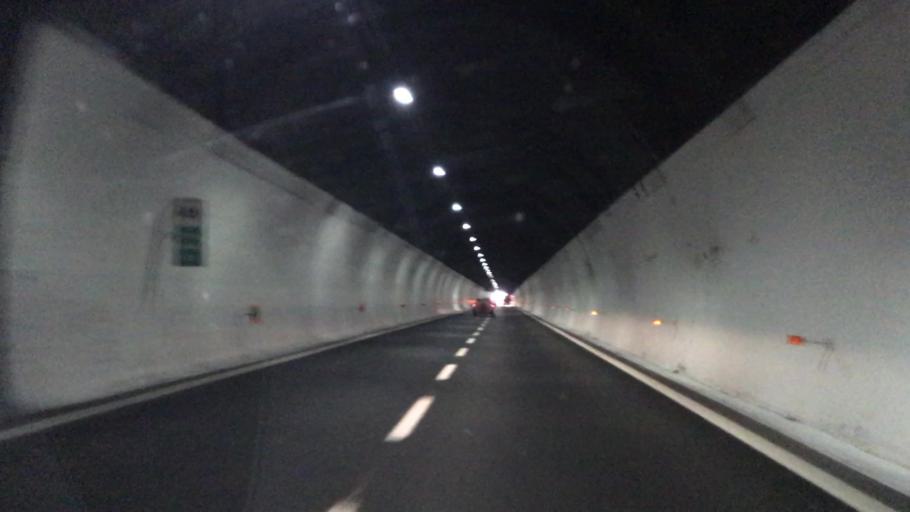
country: IT
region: Liguria
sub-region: Provincia di Genova
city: Sestri Levante
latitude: 44.2891
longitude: 9.3904
